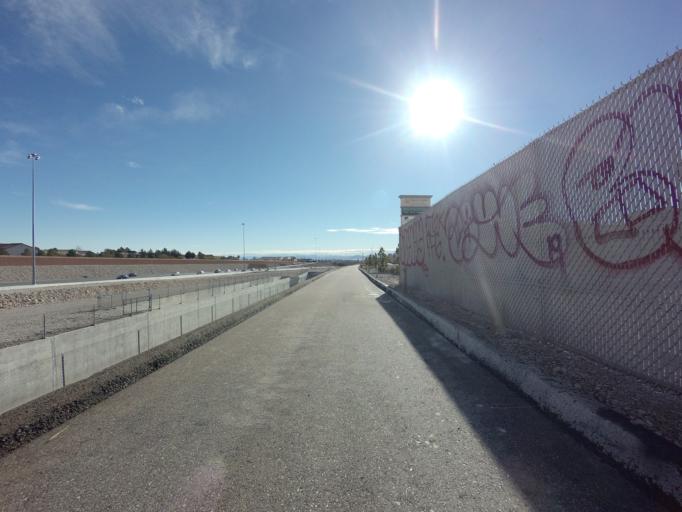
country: US
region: Nevada
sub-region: Clark County
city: Summerlin South
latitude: 36.1169
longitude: -115.3081
